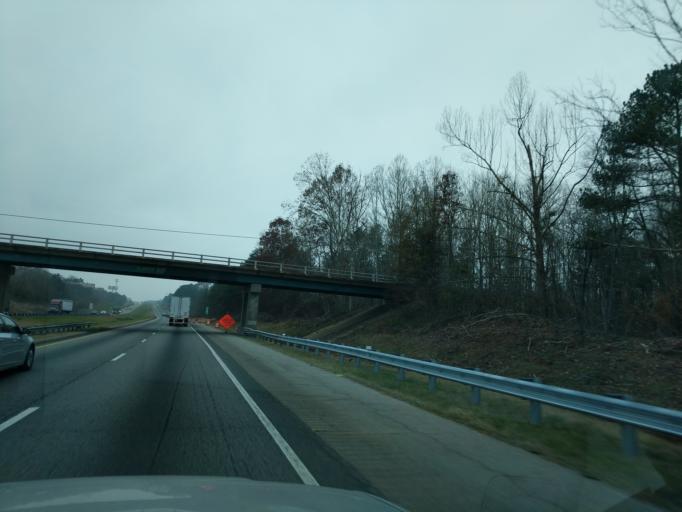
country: US
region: Georgia
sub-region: Banks County
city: Maysville
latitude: 34.1960
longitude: -83.5761
